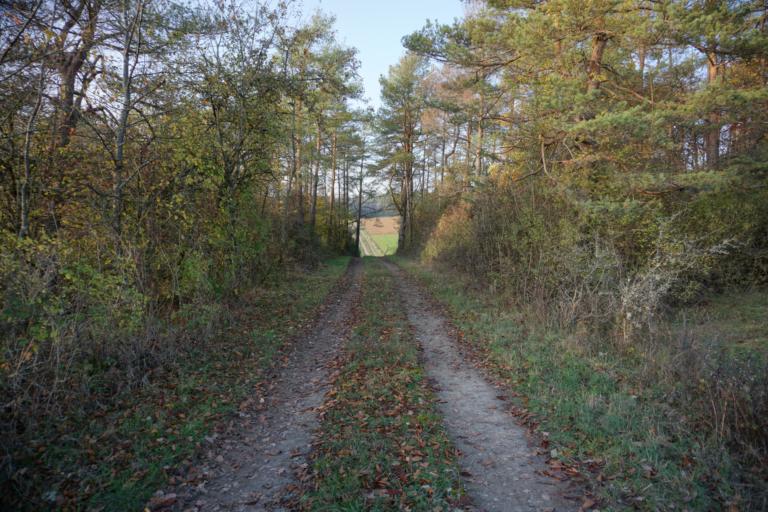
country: DE
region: Baden-Wuerttemberg
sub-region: Karlsruhe Region
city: Limbach
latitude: 49.4263
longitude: 9.2569
